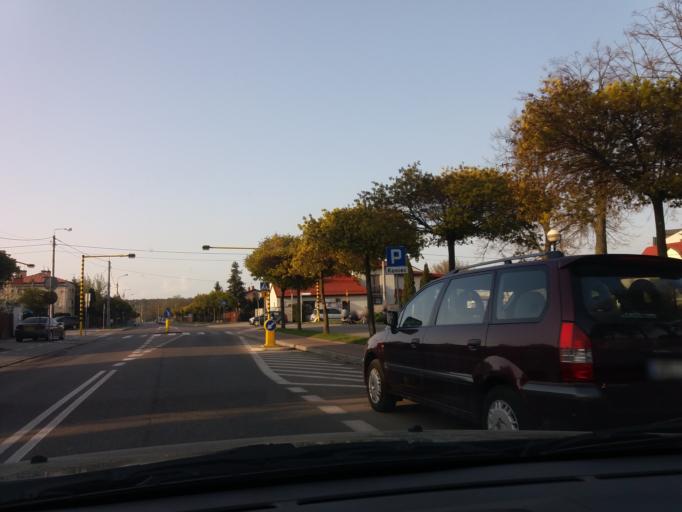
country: PL
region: Masovian Voivodeship
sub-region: Powiat mlawski
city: Mlawa
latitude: 53.1206
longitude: 20.3771
